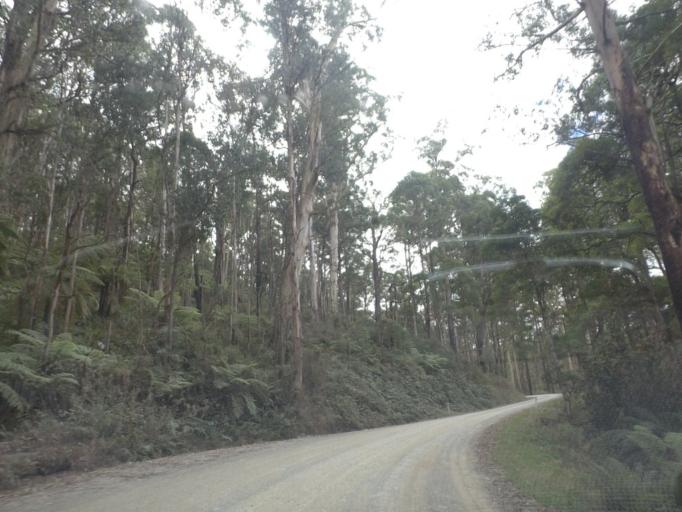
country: AU
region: Victoria
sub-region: Murrindindi
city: Alexandra
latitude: -37.4623
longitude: 145.9708
